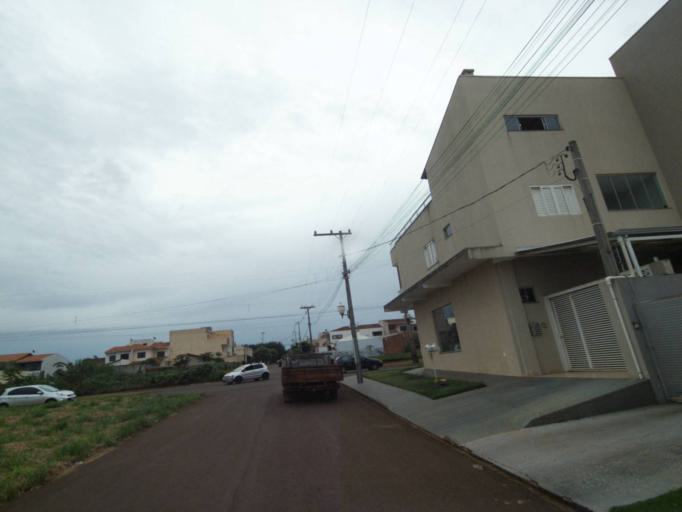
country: BR
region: Parana
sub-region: Campo Mourao
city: Campo Mourao
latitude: -24.0308
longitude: -52.3590
